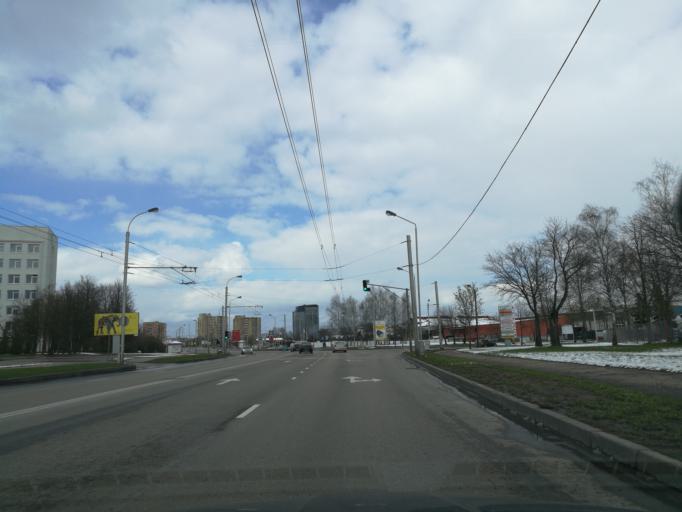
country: LT
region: Kauno apskritis
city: Dainava (Kaunas)
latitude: 54.9128
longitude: 23.9850
